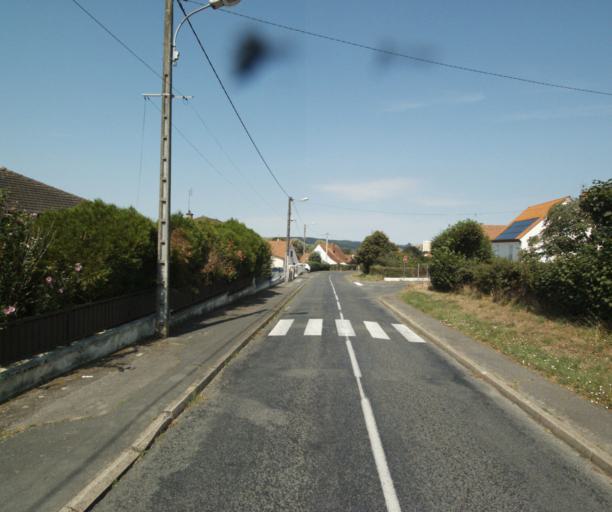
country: FR
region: Bourgogne
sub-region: Departement de Saone-et-Loire
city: Gueugnon
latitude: 46.5993
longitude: 4.0747
